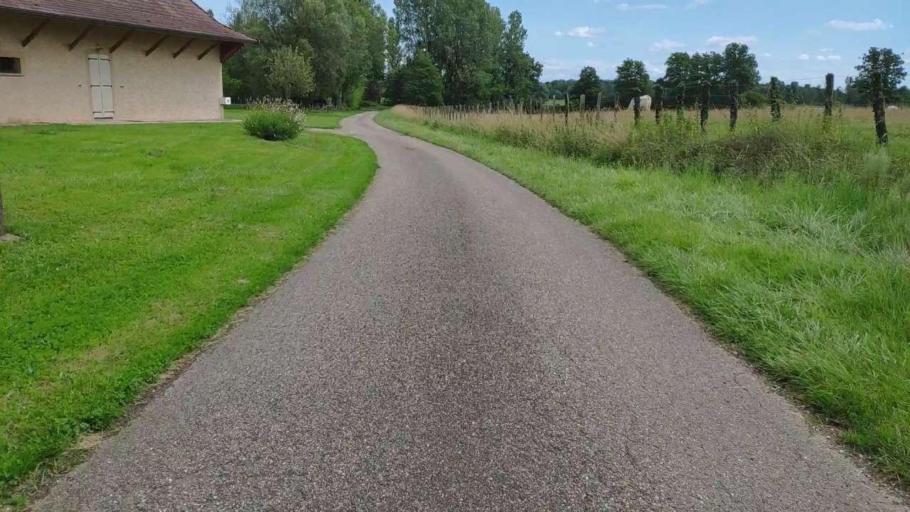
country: FR
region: Franche-Comte
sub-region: Departement du Jura
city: Chaussin
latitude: 46.8685
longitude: 5.4304
